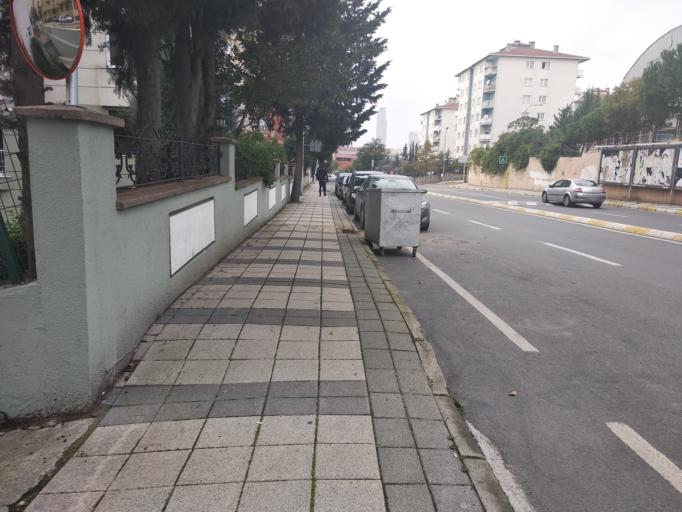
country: TR
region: Istanbul
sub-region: Atasehir
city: Atasehir
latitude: 40.9835
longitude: 29.1219
